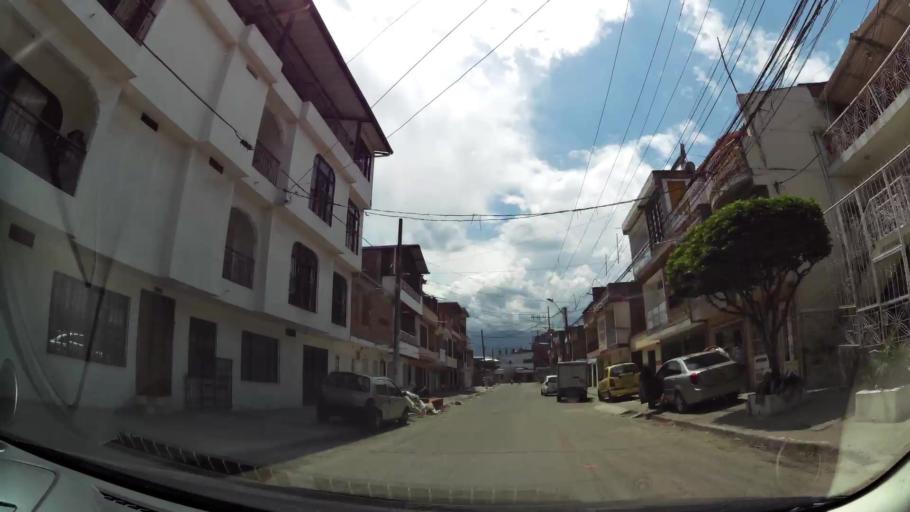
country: CO
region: Valle del Cauca
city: Cali
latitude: 3.4362
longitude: -76.5116
